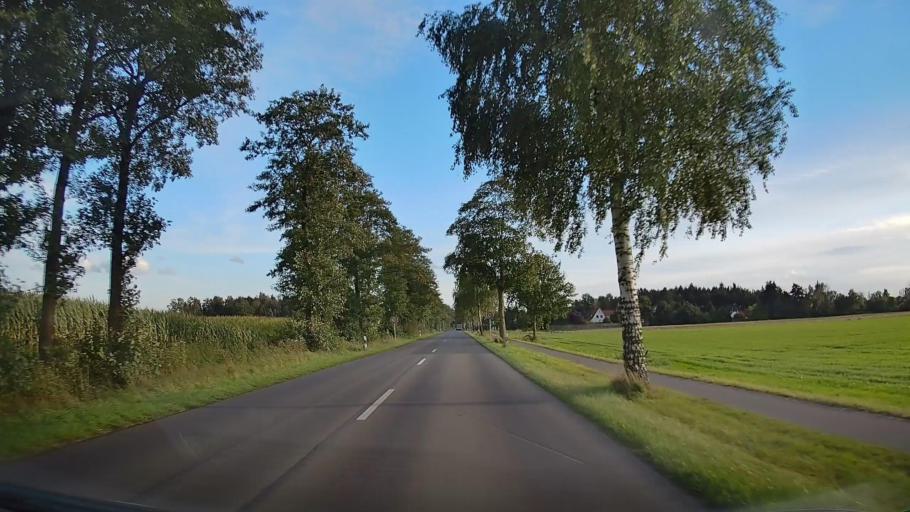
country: DE
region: Lower Saxony
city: Sottrum
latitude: 53.0945
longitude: 9.2352
